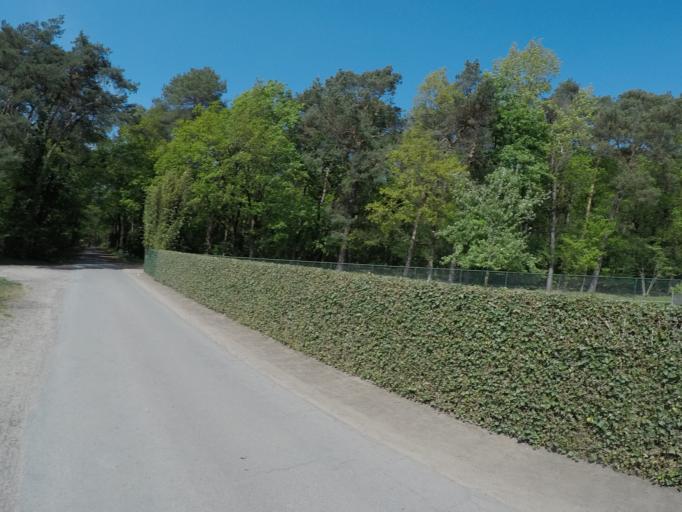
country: BE
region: Flanders
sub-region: Provincie Antwerpen
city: Zandhoven
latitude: 51.2271
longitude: 4.6278
